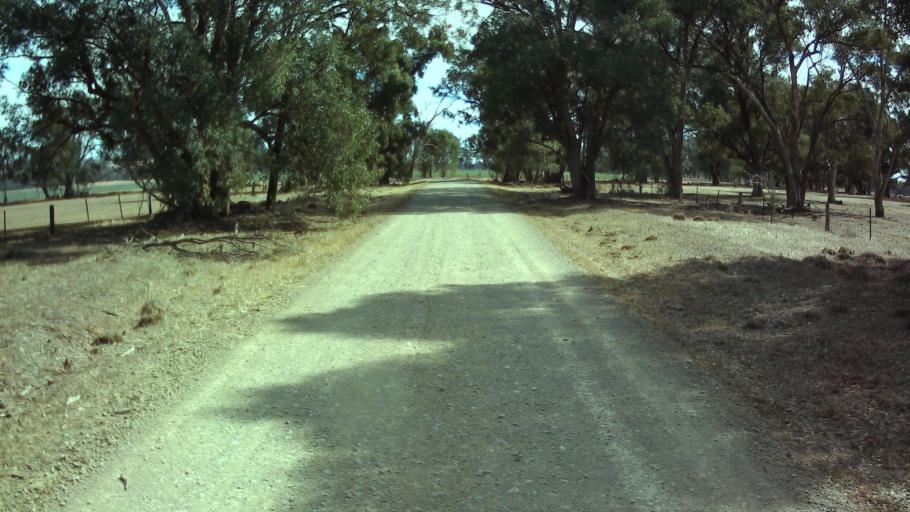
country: AU
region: New South Wales
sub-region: Weddin
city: Grenfell
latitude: -33.6881
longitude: 148.3050
